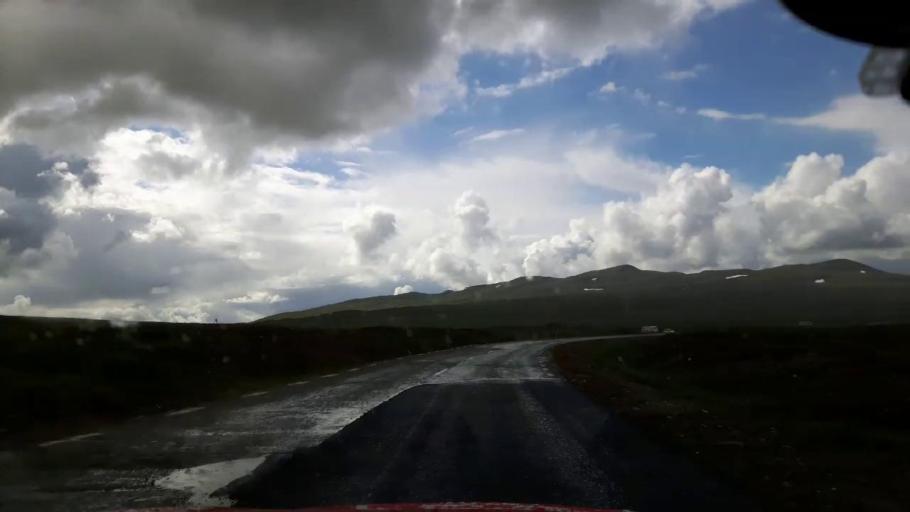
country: NO
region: Nordland
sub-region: Hattfjelldal
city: Hattfjelldal
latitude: 65.0866
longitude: 14.4581
